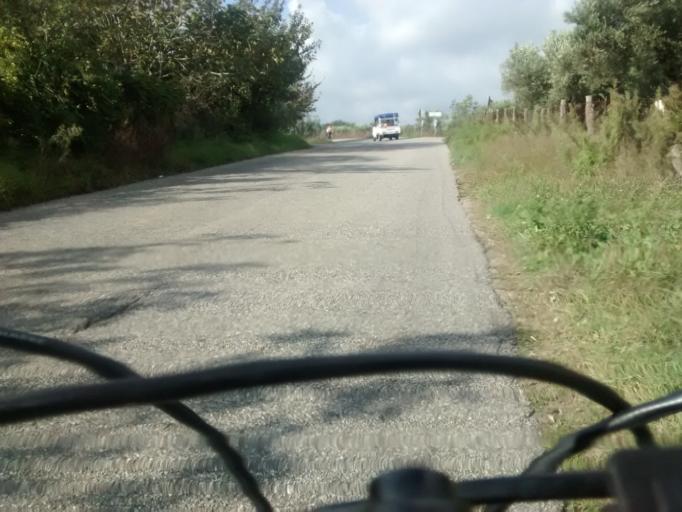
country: IT
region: Calabria
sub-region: Provincia di Catanzaro
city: Cortale
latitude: 38.8803
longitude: 16.4100
